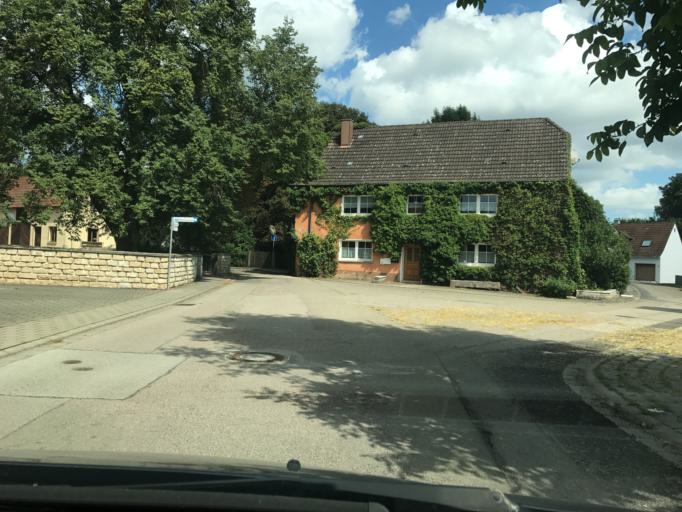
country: DE
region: Bavaria
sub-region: Regierungsbezirk Mittelfranken
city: Wittelshofen
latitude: 49.0614
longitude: 10.4808
